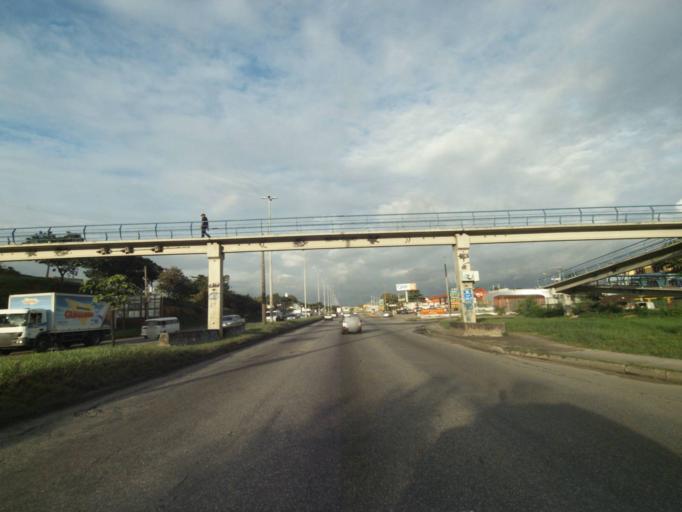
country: BR
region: Rio de Janeiro
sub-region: Nilopolis
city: Nilopolis
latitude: -22.8636
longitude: -43.4371
